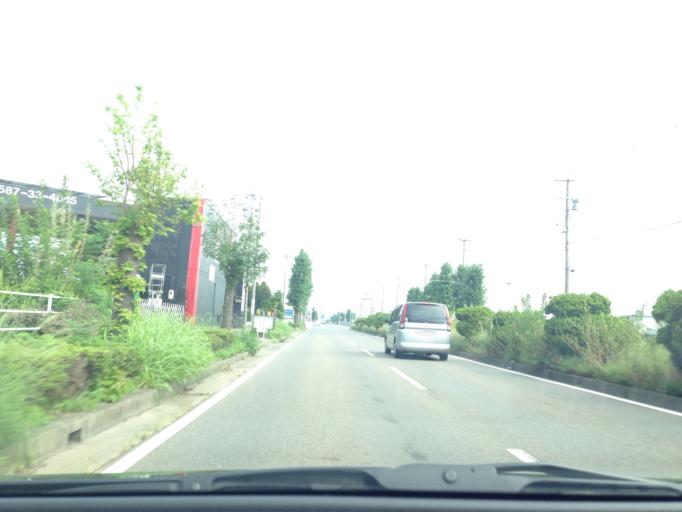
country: JP
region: Aichi
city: Inazawa
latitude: 35.2405
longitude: 136.7793
